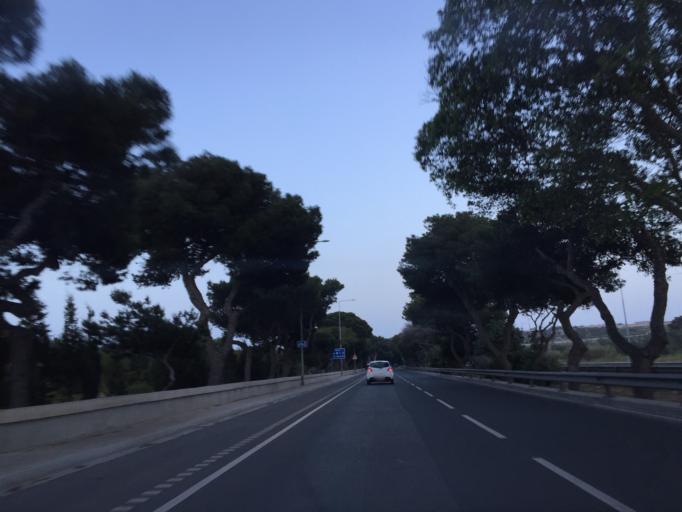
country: MT
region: Saint Paul's Bay
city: San Pawl il-Bahar
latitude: 35.9446
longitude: 14.4156
